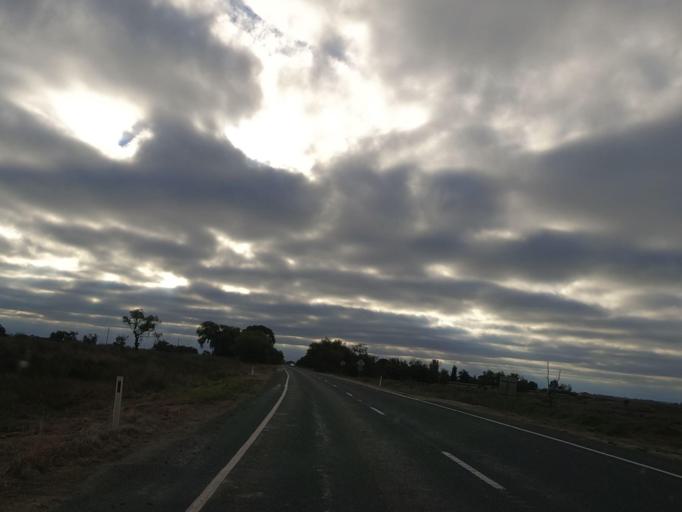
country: AU
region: Victoria
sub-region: Swan Hill
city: Swan Hill
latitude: -35.7992
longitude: 143.9546
